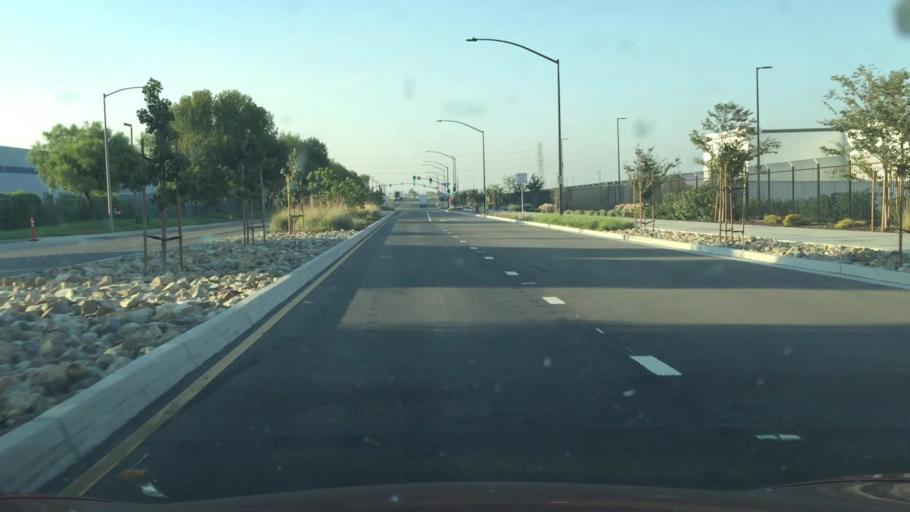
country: US
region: California
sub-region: San Joaquin County
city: Mountain House
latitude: 37.7255
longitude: -121.5313
